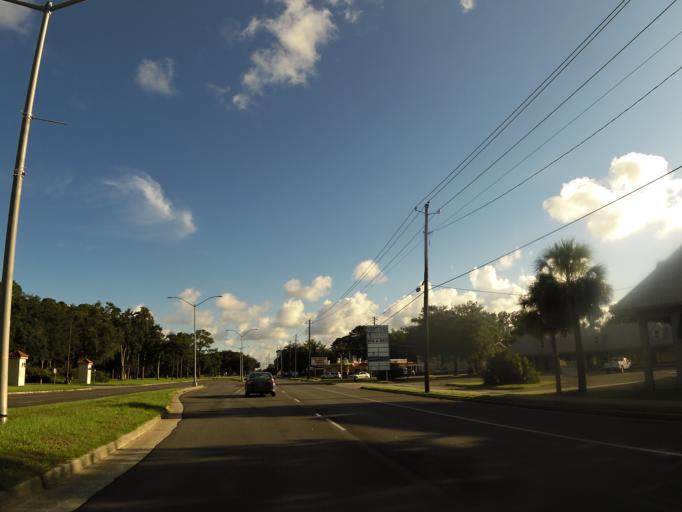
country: US
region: Georgia
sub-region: Glynn County
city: Brunswick
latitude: 31.1820
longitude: -81.4890
